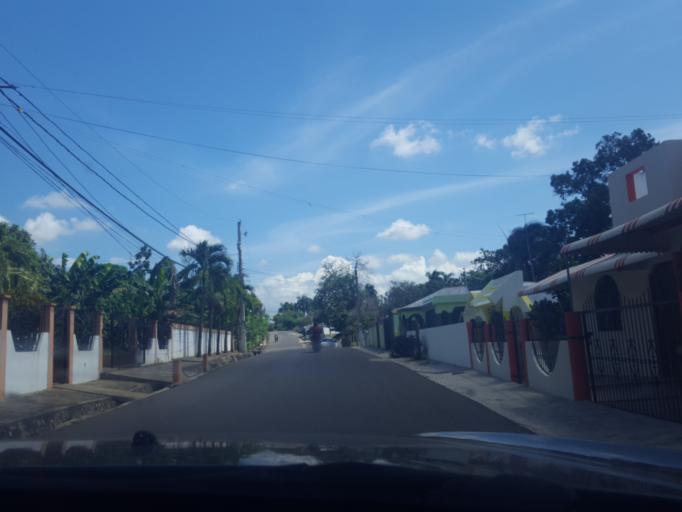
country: DO
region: Santiago
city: Baitoa
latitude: 19.3760
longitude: -70.6518
